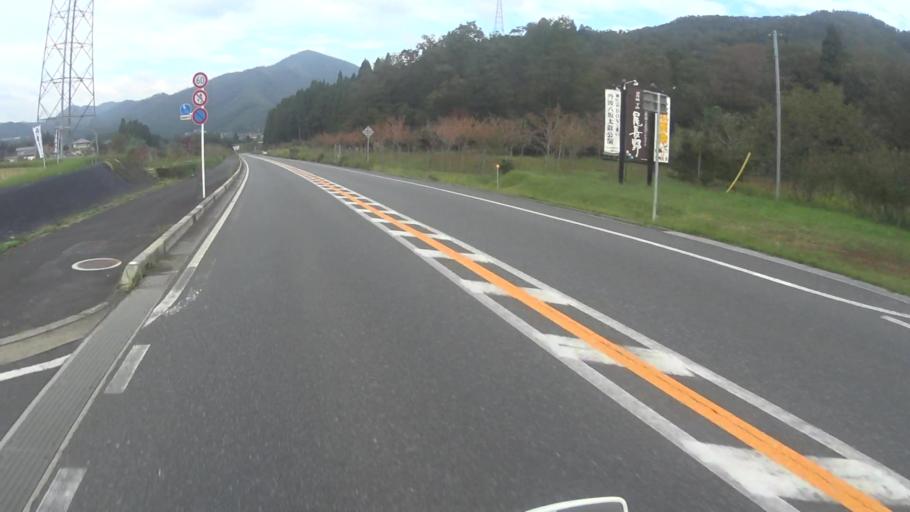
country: JP
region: Kyoto
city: Ayabe
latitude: 35.2173
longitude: 135.4270
